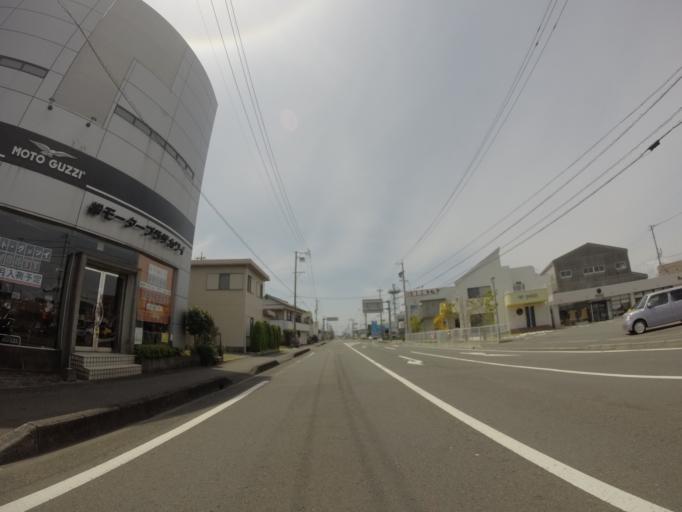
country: JP
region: Shizuoka
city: Yaizu
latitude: 34.8369
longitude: 138.3092
